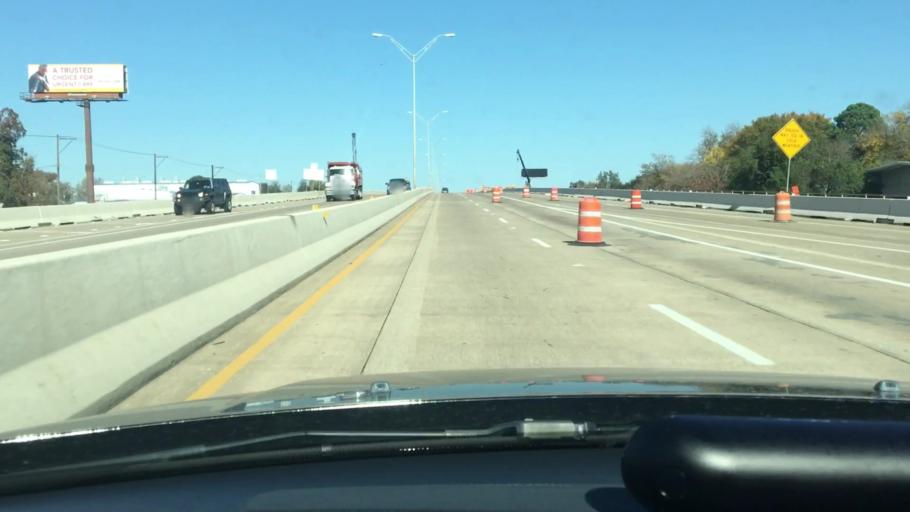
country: US
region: Texas
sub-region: Harris County
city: Deer Park
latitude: 29.6732
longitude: -95.1560
